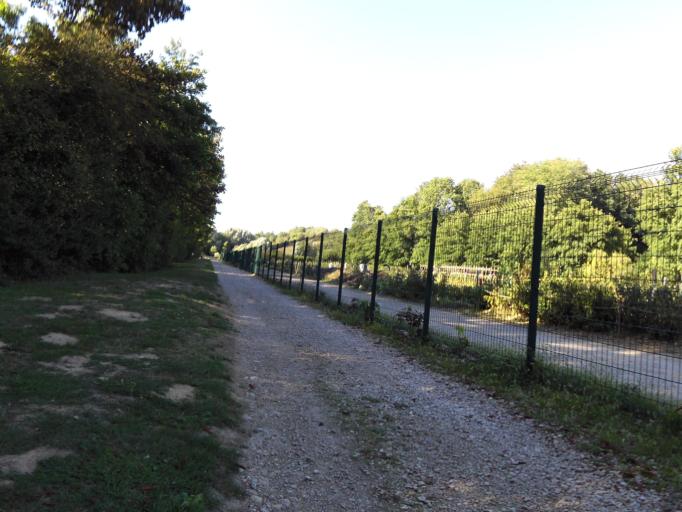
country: FR
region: Rhone-Alpes
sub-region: Departement de l'Ain
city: Meximieux
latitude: 45.9032
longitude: 5.1846
